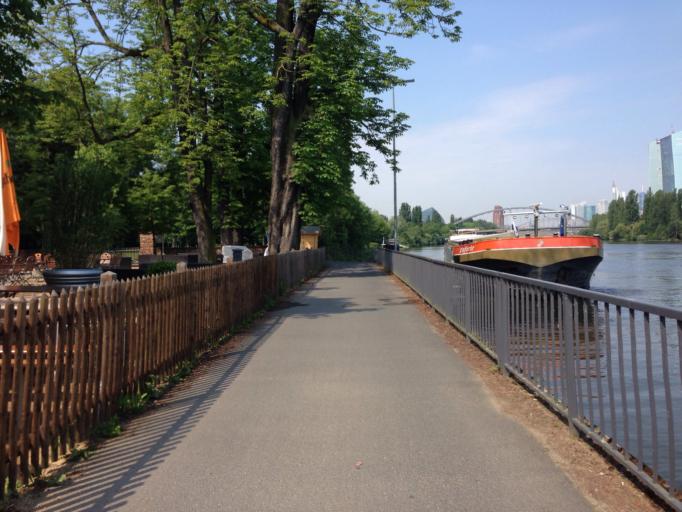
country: DE
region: Hesse
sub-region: Regierungsbezirk Darmstadt
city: Frankfurt am Main
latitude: 50.1063
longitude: 8.7215
